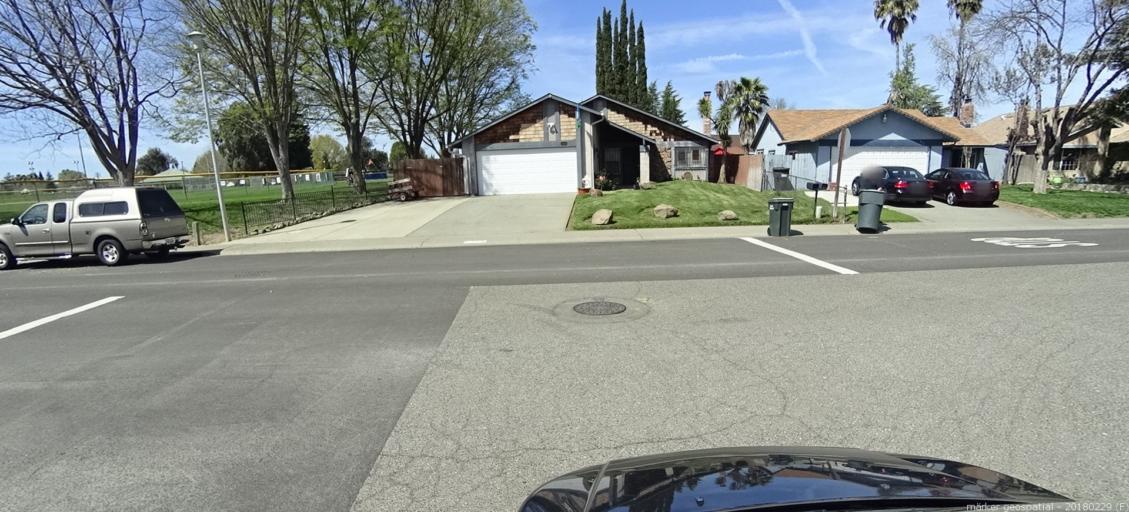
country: US
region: California
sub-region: Sacramento County
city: Rosemont
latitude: 38.5512
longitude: -121.3496
